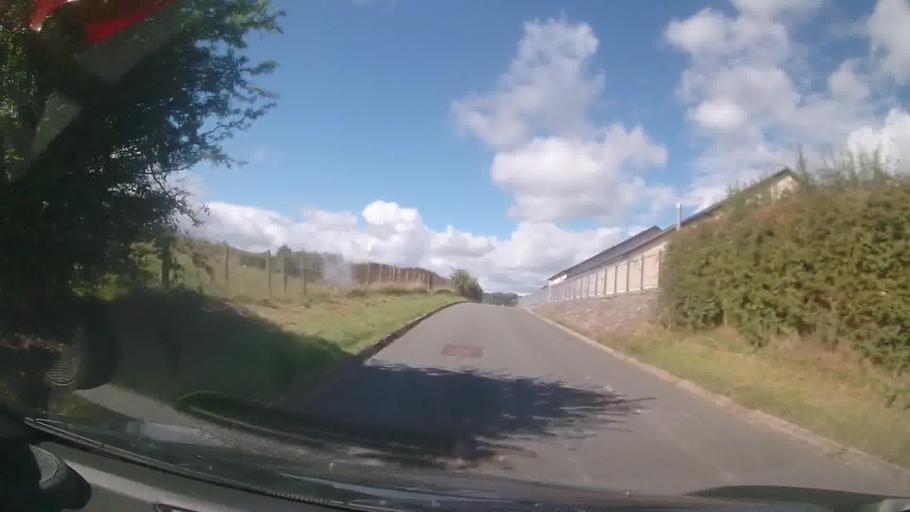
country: GB
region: Wales
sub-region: Merthyr Tydfil County Borough
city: Merthyr Tydfil
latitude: 51.7773
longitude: -3.3646
